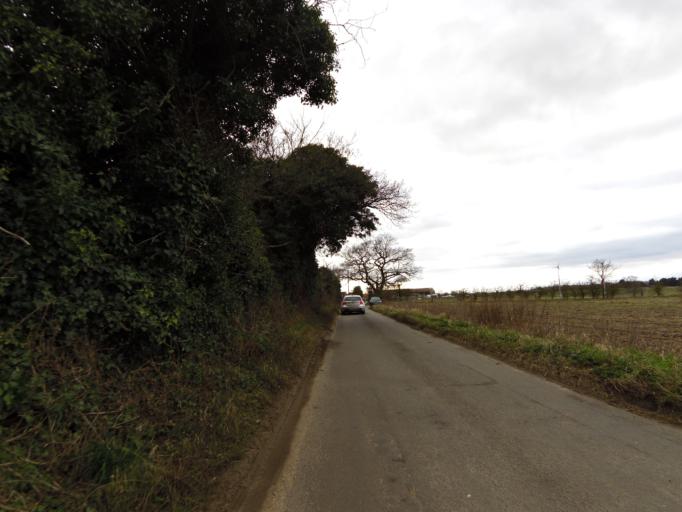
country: GB
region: England
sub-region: Suffolk
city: Woodbridge
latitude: 52.0262
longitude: 1.3028
